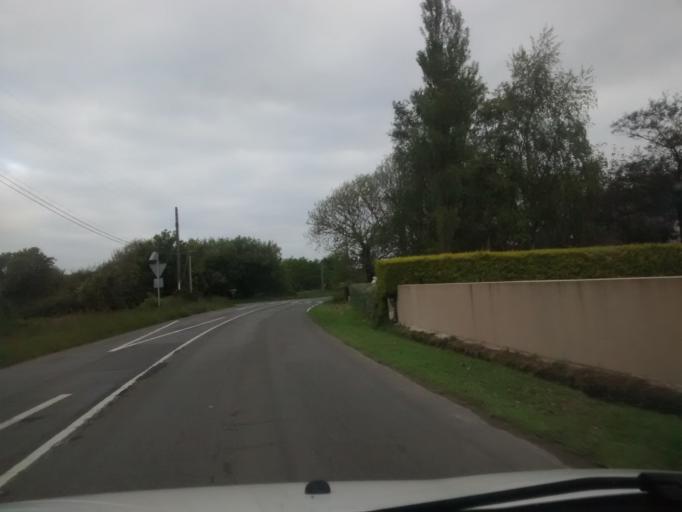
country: FR
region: Brittany
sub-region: Departement des Cotes-d'Armor
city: Tregastel
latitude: 48.8020
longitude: -3.4738
